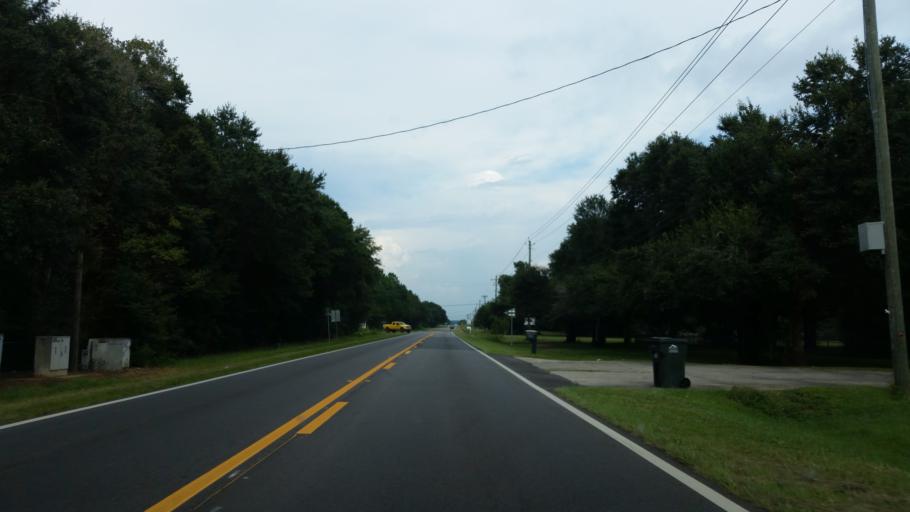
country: US
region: Florida
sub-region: Santa Rosa County
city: Wallace
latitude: 30.6474
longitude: -87.1581
